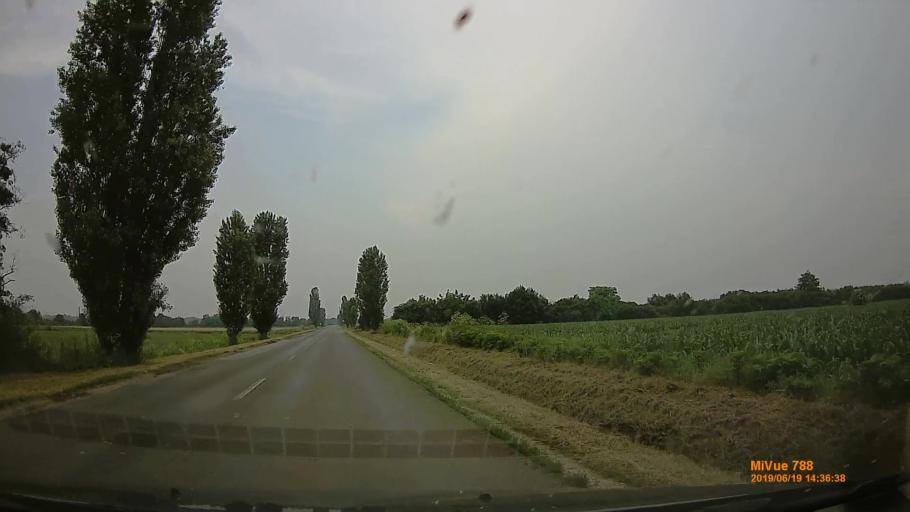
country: HU
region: Baranya
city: Szigetvar
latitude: 46.0622
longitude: 17.7737
